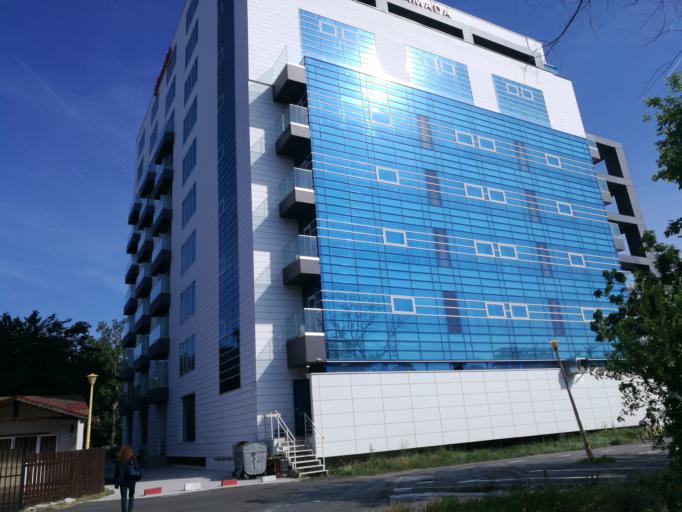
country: RO
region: Constanta
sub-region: Municipiul Constanta
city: Palazu Mare
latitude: 44.2170
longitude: 28.6321
